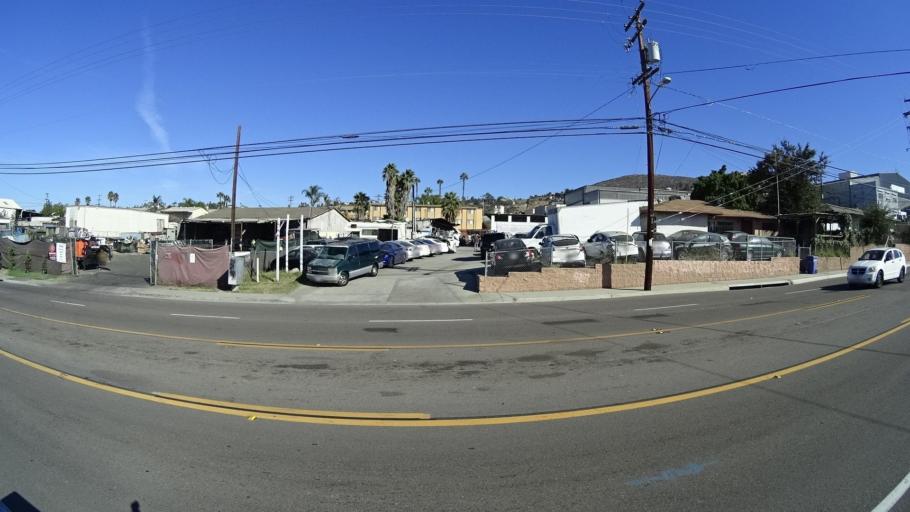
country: US
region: California
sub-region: San Diego County
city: La Presa
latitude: 32.7151
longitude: -117.0001
